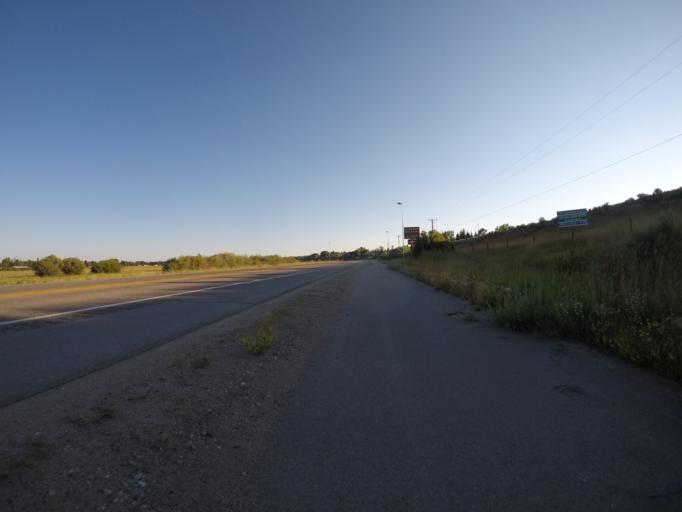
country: US
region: Wyoming
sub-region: Sublette County
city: Pinedale
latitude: 42.8541
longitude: -109.8503
